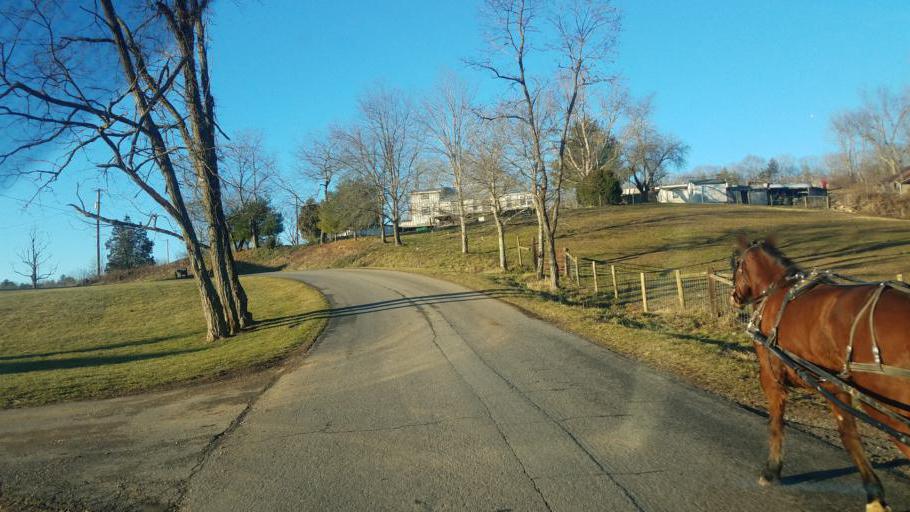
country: US
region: Virginia
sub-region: Pulaski County
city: Pulaski
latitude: 37.1746
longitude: -80.8598
